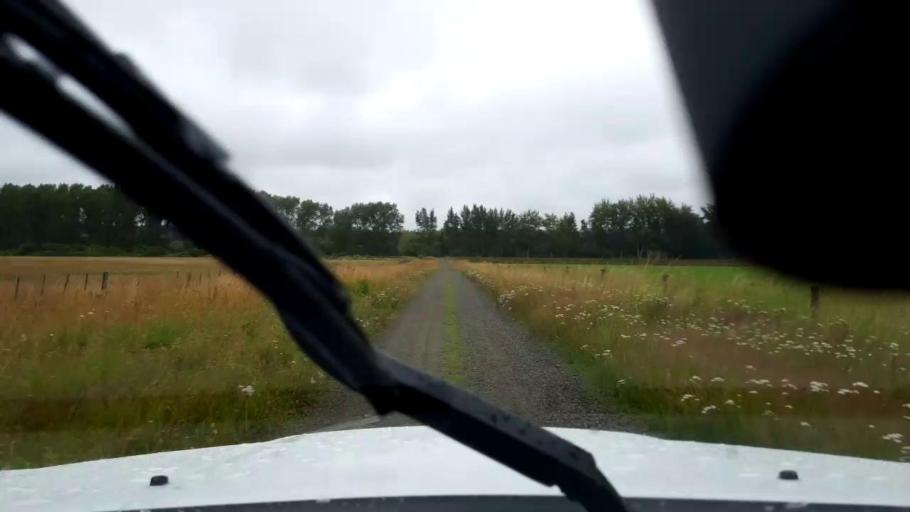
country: NZ
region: Canterbury
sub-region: Timaru District
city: Pleasant Point
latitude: -44.2580
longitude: 171.1989
